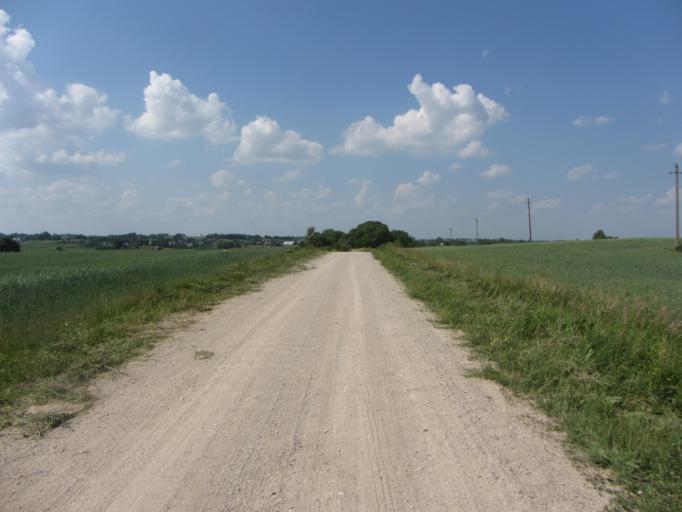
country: LT
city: Lazdijai
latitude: 54.2215
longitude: 23.5678
